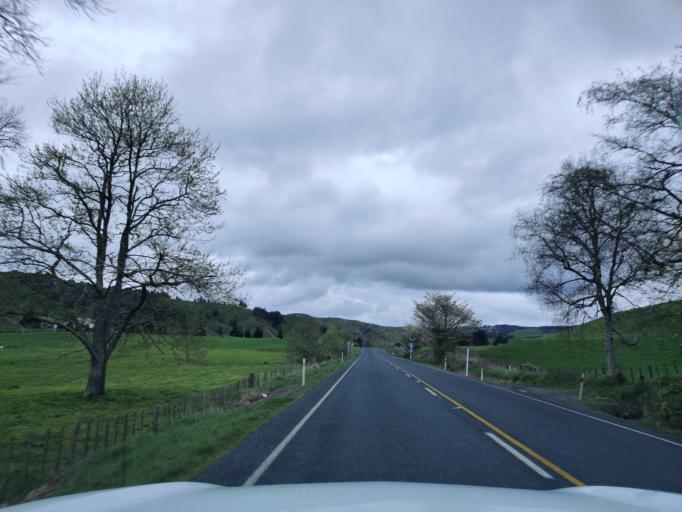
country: NZ
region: Waikato
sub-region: Otorohanga District
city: Otorohanga
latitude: -38.5217
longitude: 175.1792
